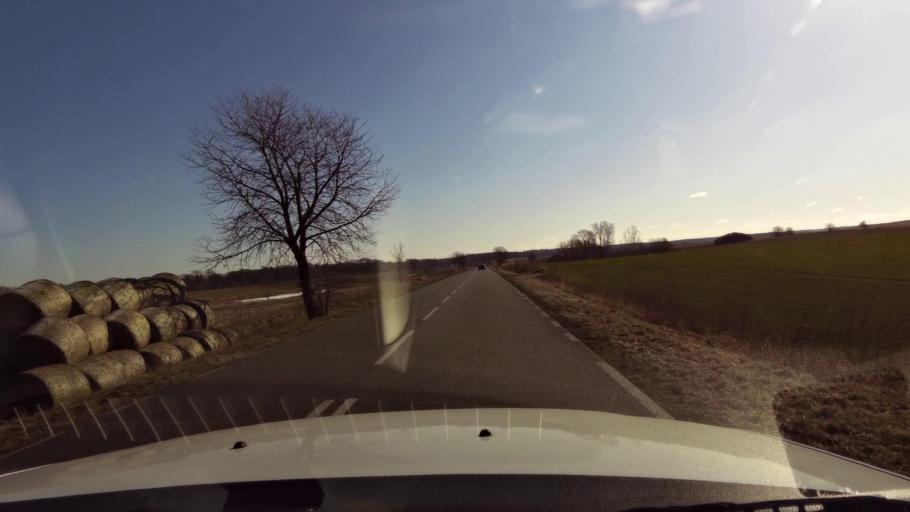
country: PL
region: West Pomeranian Voivodeship
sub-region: Powiat mysliborski
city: Nowogrodek Pomorski
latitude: 52.9877
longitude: 15.1068
